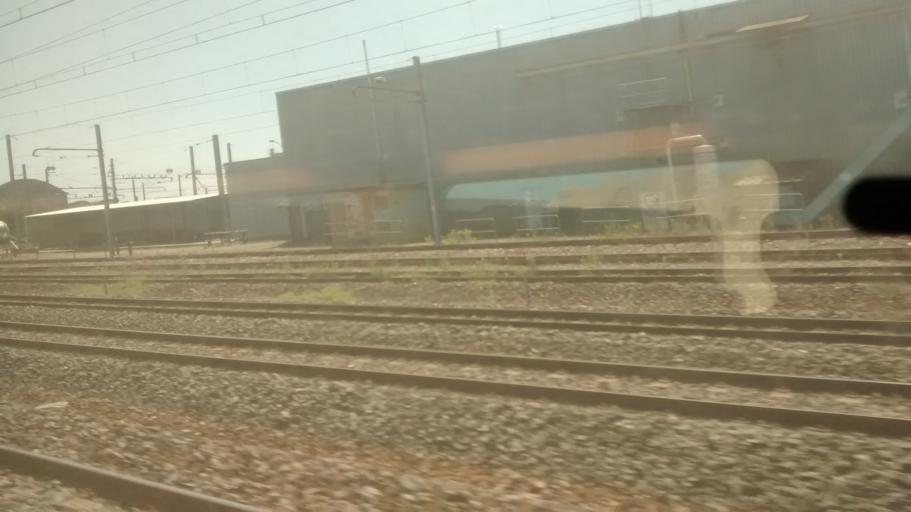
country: FR
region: Rhone-Alpes
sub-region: Departement du Rhone
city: Venissieux
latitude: 45.7121
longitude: 4.8701
